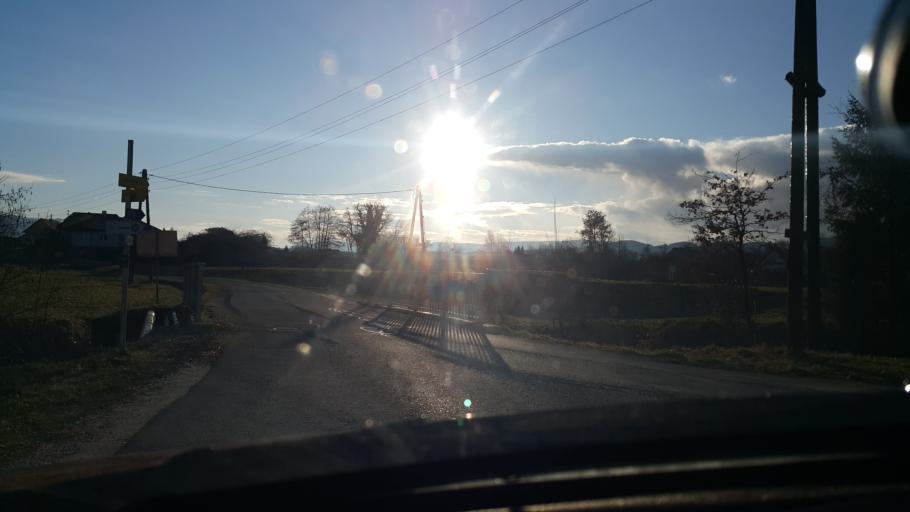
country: AT
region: Styria
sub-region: Politischer Bezirk Deutschlandsberg
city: Sankt Martin im Sulmtal
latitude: 46.7698
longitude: 15.2820
